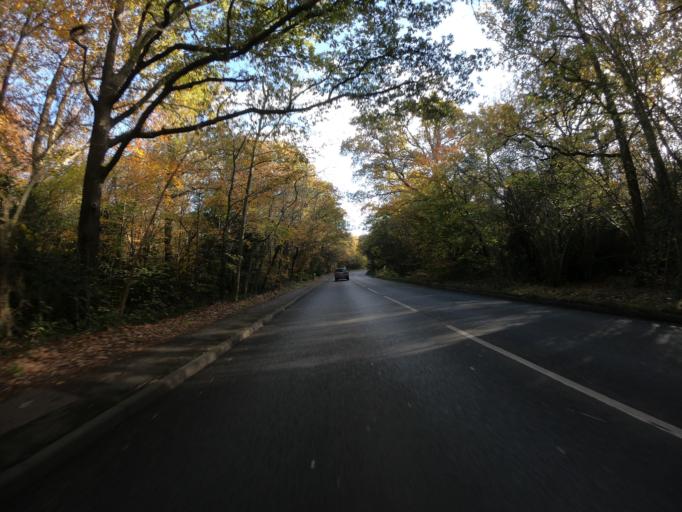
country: GB
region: England
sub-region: Greater London
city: Chislehurst
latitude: 51.4046
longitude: 0.0844
